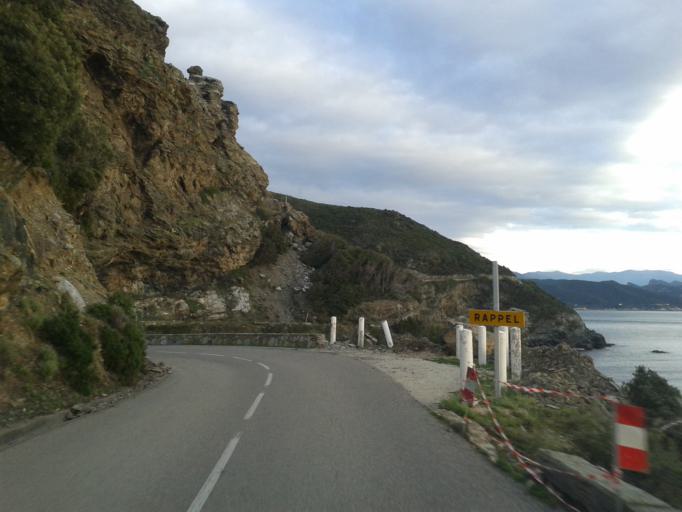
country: FR
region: Corsica
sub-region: Departement de la Haute-Corse
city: Saint-Florent
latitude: 42.7635
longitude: 9.3380
